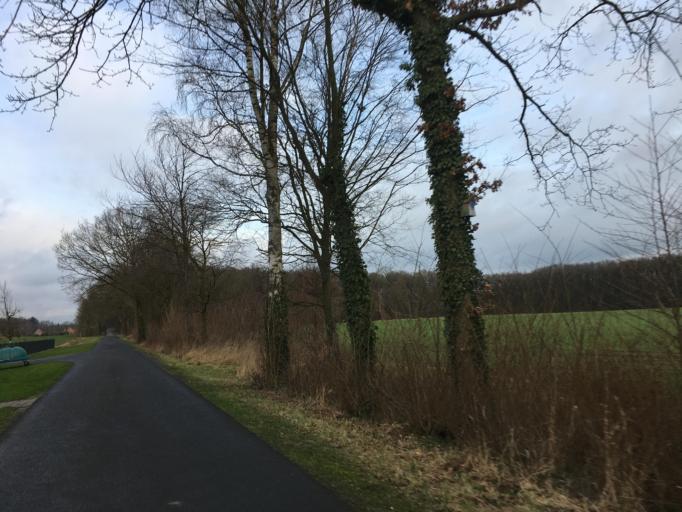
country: DE
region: North Rhine-Westphalia
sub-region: Regierungsbezirk Munster
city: Senden
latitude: 51.9168
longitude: 7.4967
